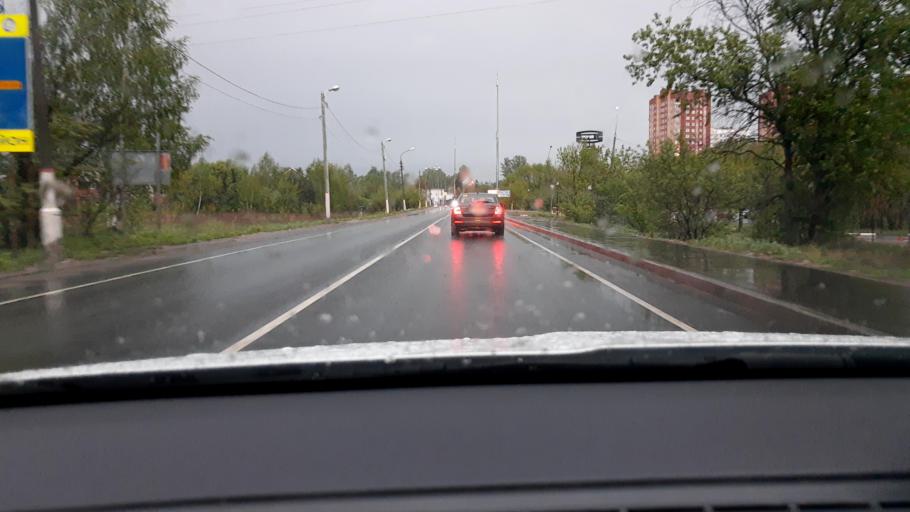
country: RU
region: Moskovskaya
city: Zagoryanskiy
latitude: 55.9284
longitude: 37.9503
